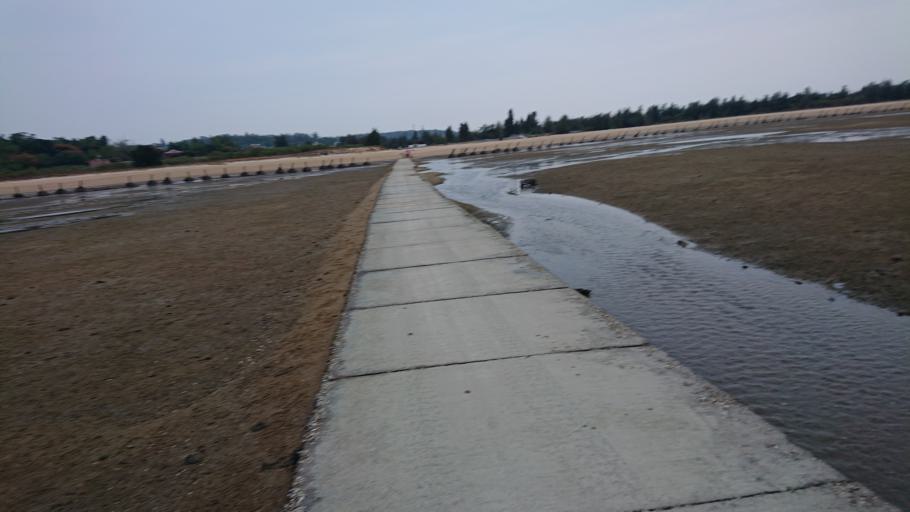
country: TW
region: Fukien
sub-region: Kinmen
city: Jincheng
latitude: 24.4304
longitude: 118.2253
